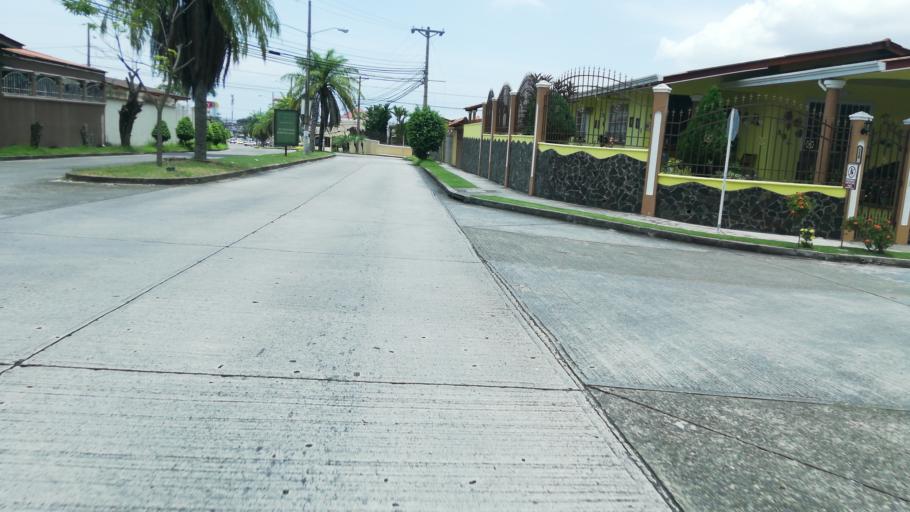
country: PA
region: Panama
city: San Miguelito
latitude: 9.0723
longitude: -79.4521
